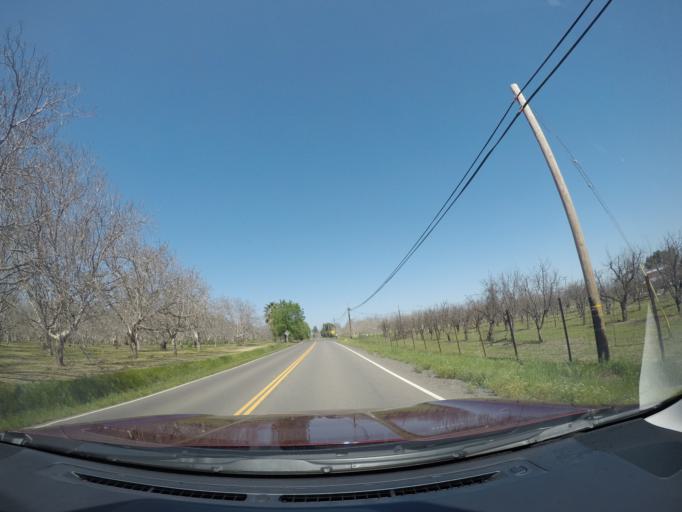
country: US
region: California
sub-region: Yolo County
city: Winters
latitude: 38.4944
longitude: -121.9515
